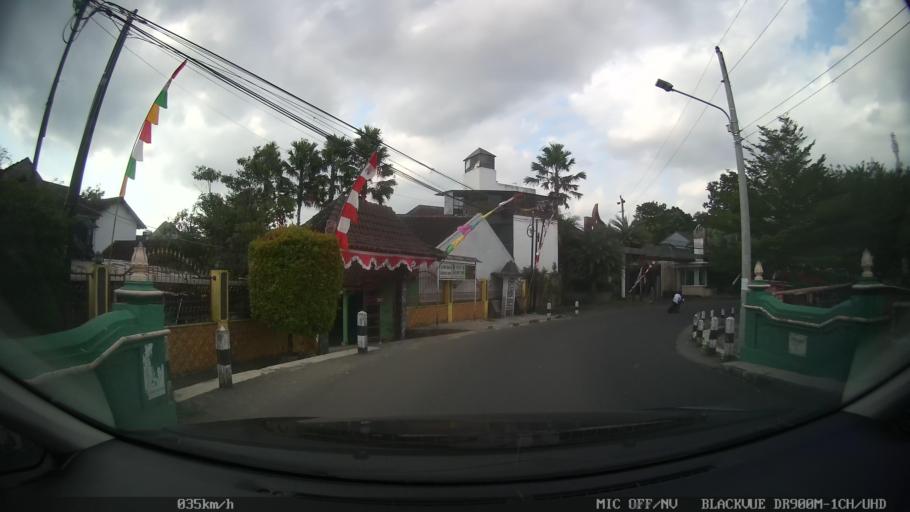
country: ID
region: Daerah Istimewa Yogyakarta
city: Gamping Lor
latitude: -7.7829
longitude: 110.3367
